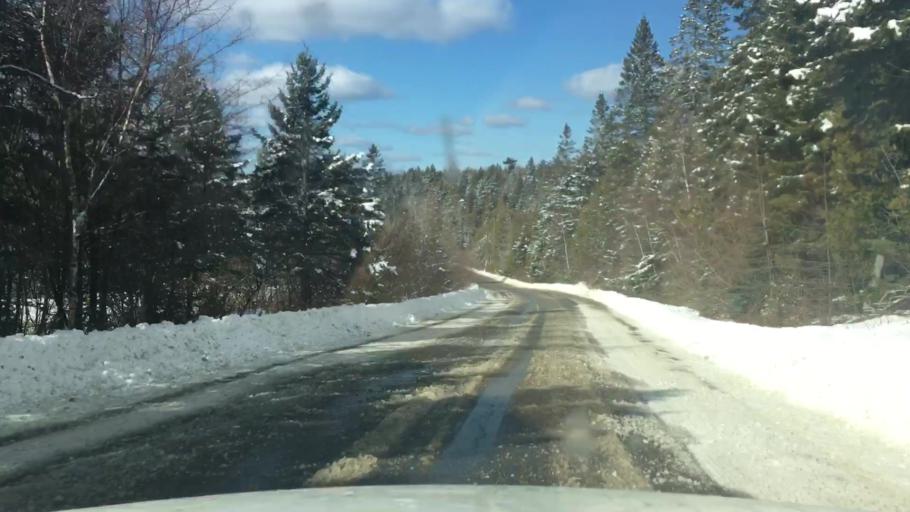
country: US
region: Maine
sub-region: Washington County
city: Machias
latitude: 44.6823
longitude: -67.4565
